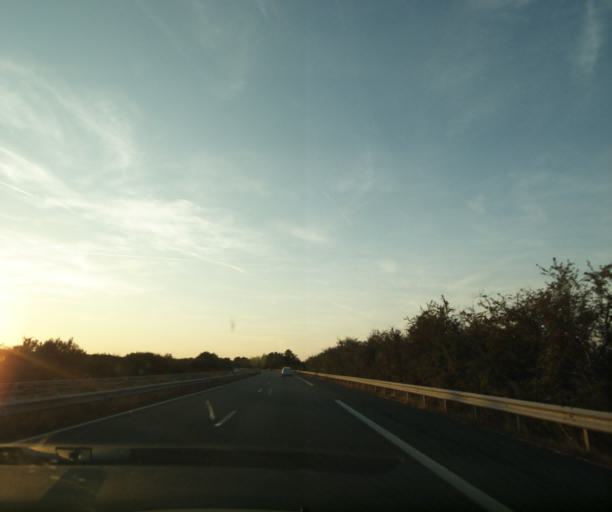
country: FR
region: Aquitaine
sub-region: Departement du Lot-et-Garonne
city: Tonneins
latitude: 44.3731
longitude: 0.2356
